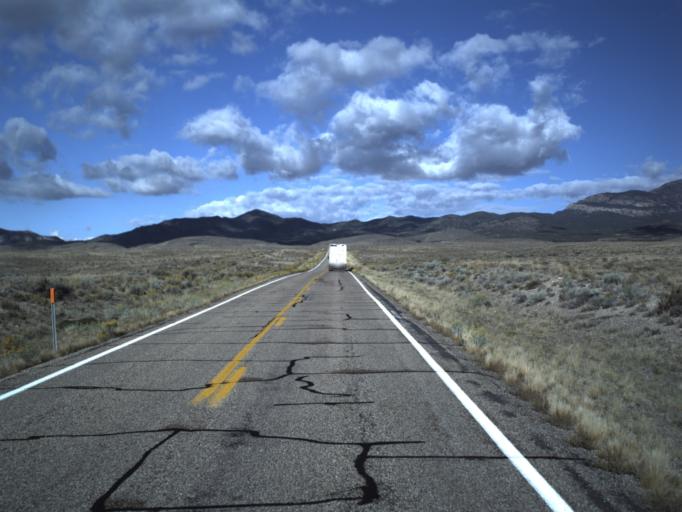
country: US
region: Utah
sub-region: Beaver County
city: Milford
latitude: 38.4473
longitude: -113.1878
